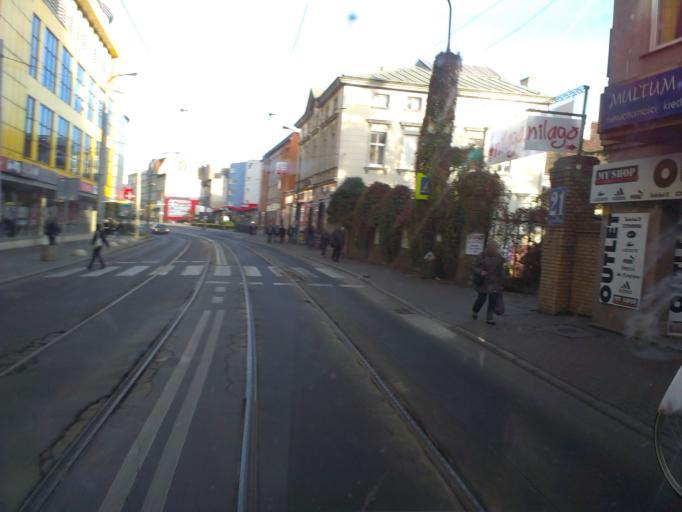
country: PL
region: Lubusz
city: Gorzow Wielkopolski
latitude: 52.7300
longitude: 15.2335
